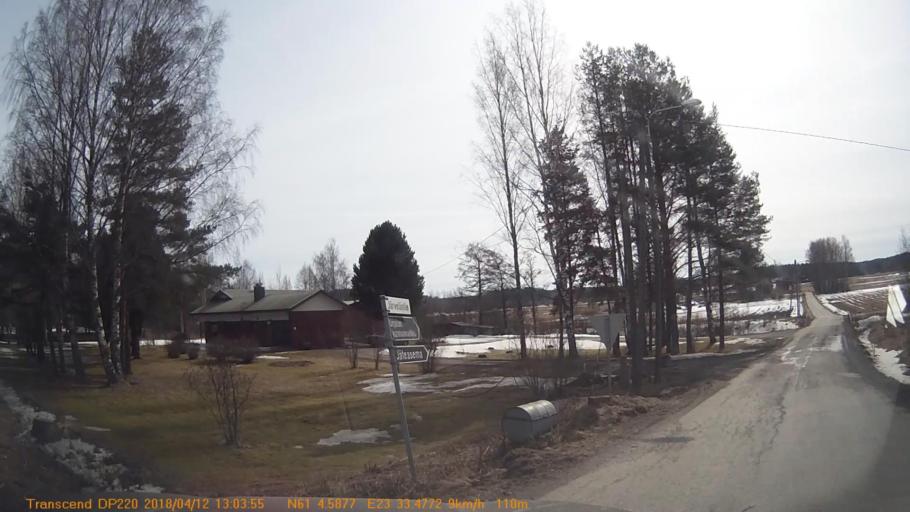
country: FI
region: Pirkanmaa
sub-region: Etelae-Pirkanmaa
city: Urjala
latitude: 61.0757
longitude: 23.5584
